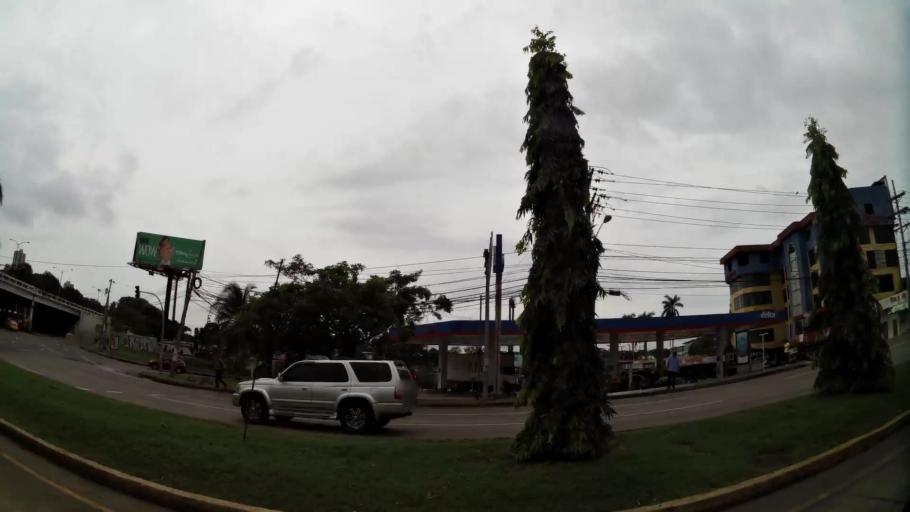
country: PA
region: Panama
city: Panama
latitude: 8.9892
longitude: -79.5331
